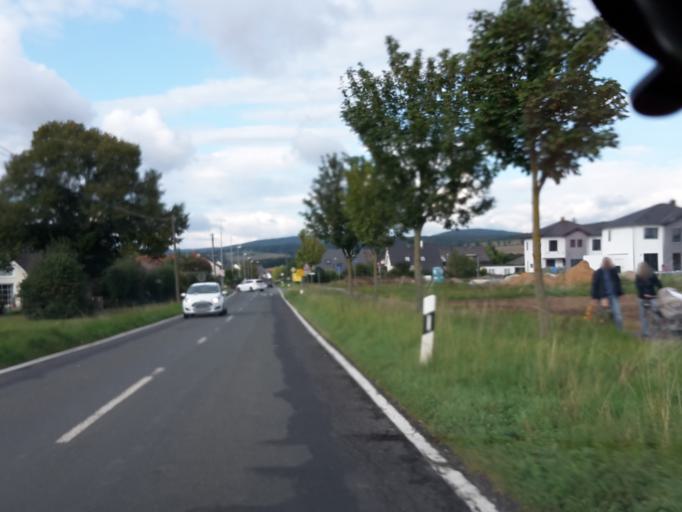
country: DE
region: Hesse
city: Bad Camberg
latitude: 50.2650
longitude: 8.2759
